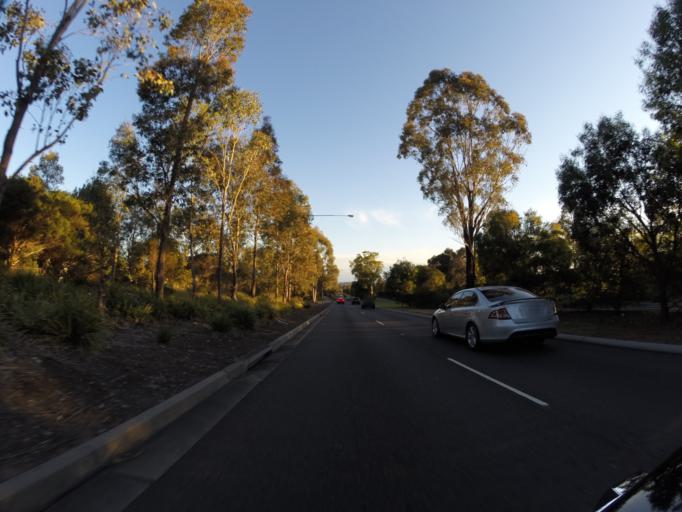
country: AU
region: New South Wales
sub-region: Fairfield
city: Cecil Park
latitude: -33.8901
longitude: 150.8602
